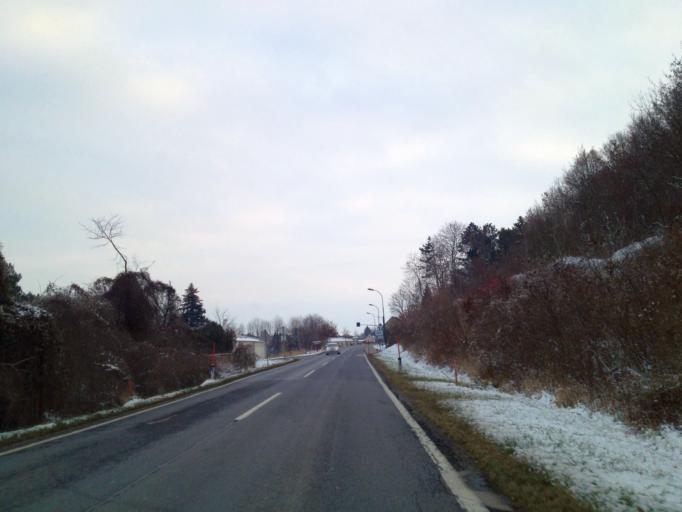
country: AT
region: Lower Austria
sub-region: Politischer Bezirk Bruck an der Leitha
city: Berg
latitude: 48.1080
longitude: 17.0419
